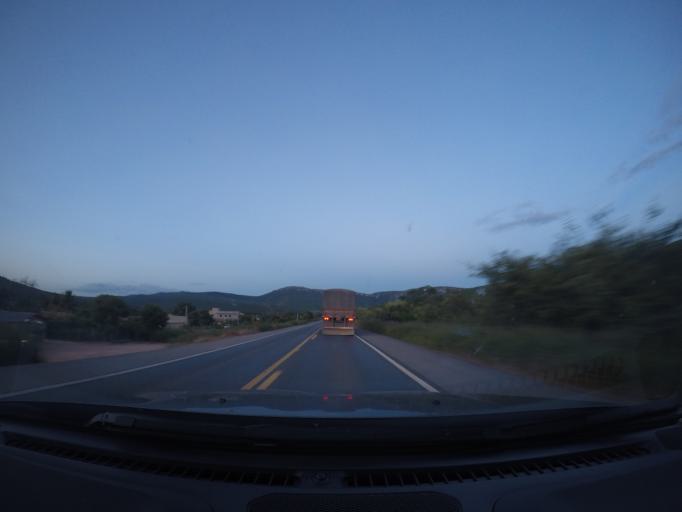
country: BR
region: Bahia
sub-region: Seabra
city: Seabra
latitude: -12.4823
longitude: -41.7202
